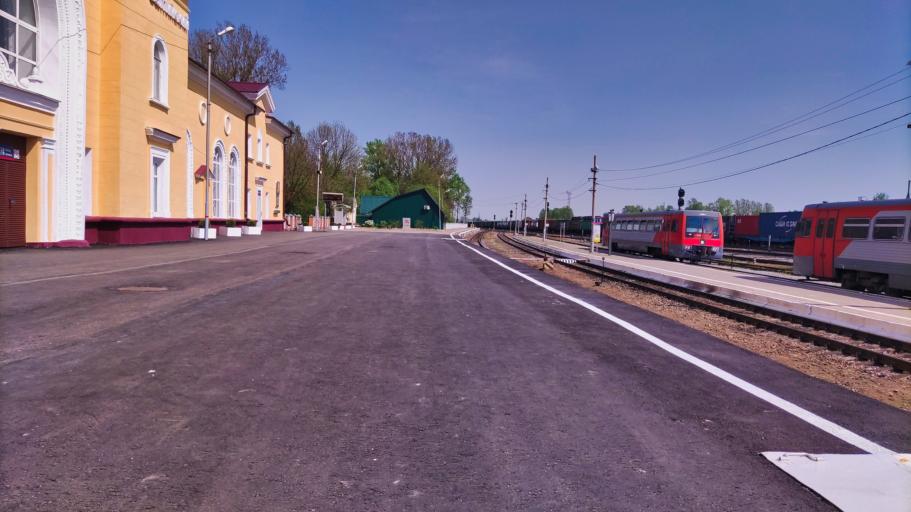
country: RU
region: Tverskaya
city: Rzhev
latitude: 56.2396
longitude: 34.3204
